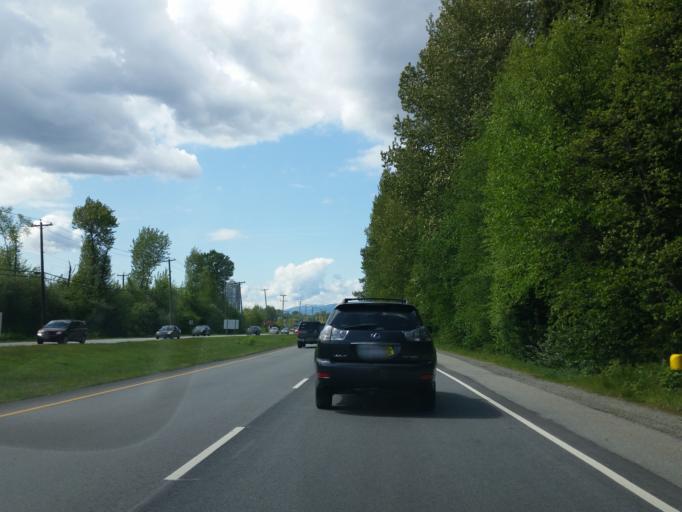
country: CA
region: British Columbia
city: Coquitlam
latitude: 49.2621
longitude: -122.7629
